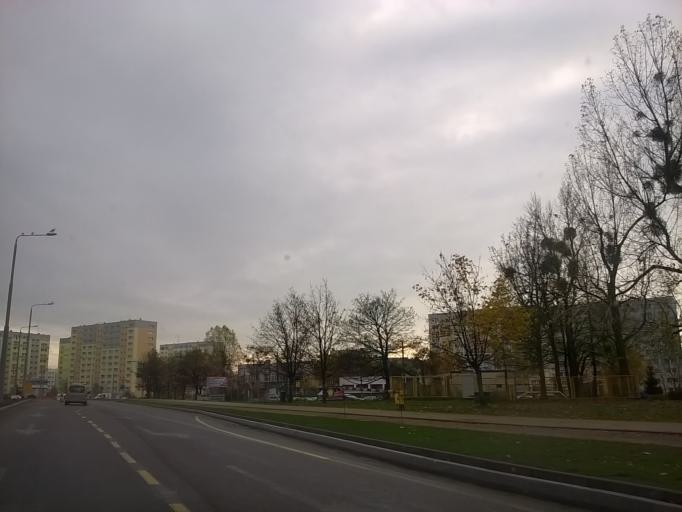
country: PL
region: Pomeranian Voivodeship
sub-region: Powiat gdanski
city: Kowale
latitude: 54.3591
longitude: 18.5786
